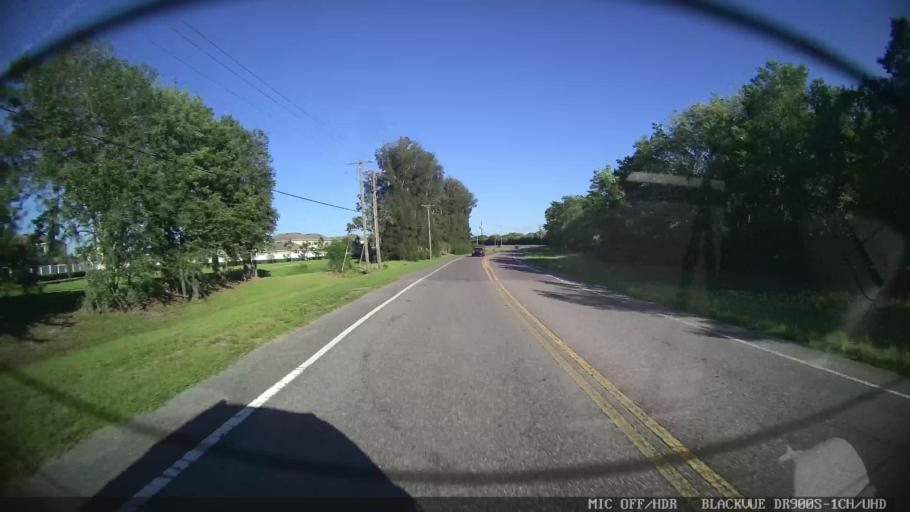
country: US
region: Florida
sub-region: Hillsborough County
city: Sun City Center
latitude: 27.7425
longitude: -82.3417
